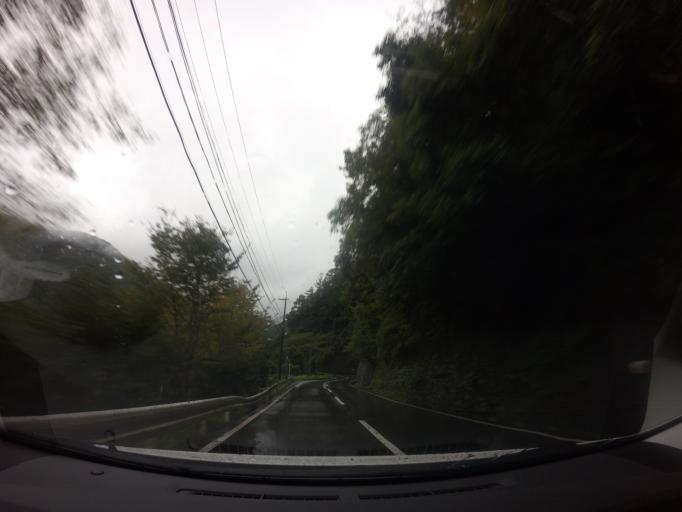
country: JP
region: Wakayama
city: Koya
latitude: 34.0613
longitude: 135.7495
